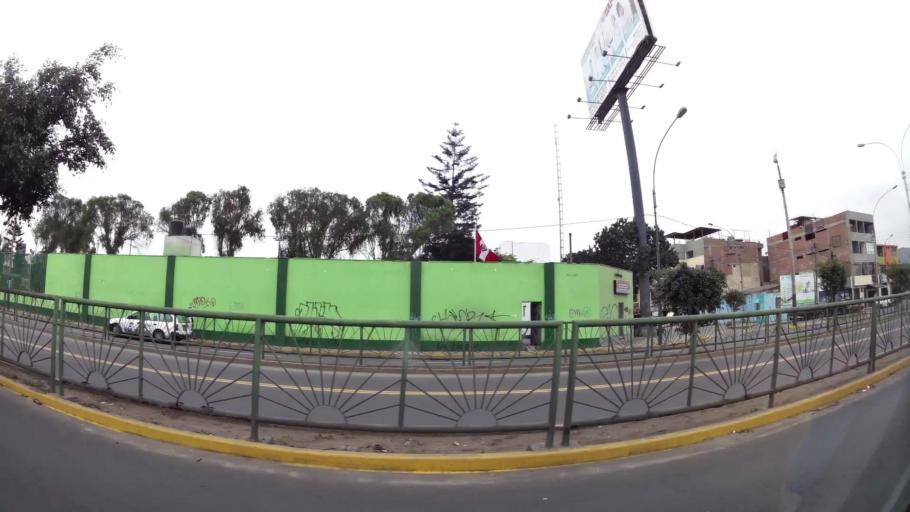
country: PE
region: Lima
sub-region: Lima
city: Surco
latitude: -12.1153
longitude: -77.0093
